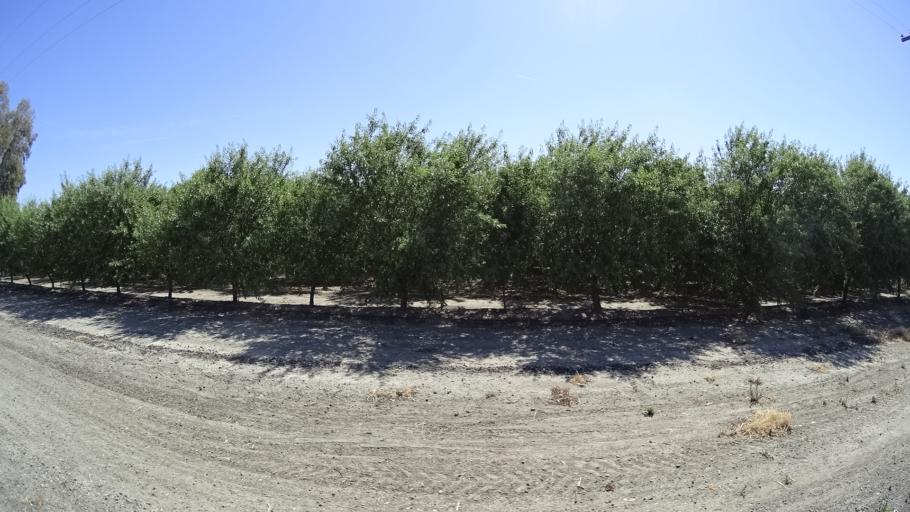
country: US
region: California
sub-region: Kings County
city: Stratford
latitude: 36.1656
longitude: -119.7802
